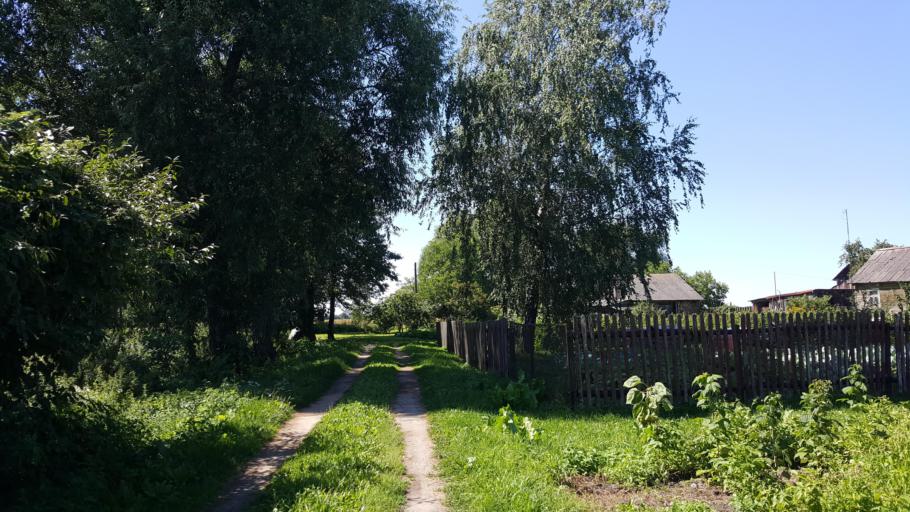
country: BY
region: Brest
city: Charnawchytsy
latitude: 52.2131
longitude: 23.7974
